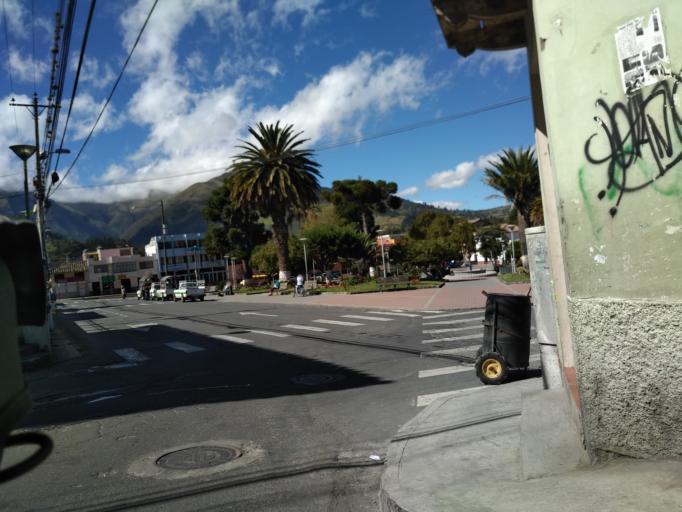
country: EC
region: Imbabura
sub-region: Canton Otavalo
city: Otavalo
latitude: 0.1968
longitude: -78.1908
